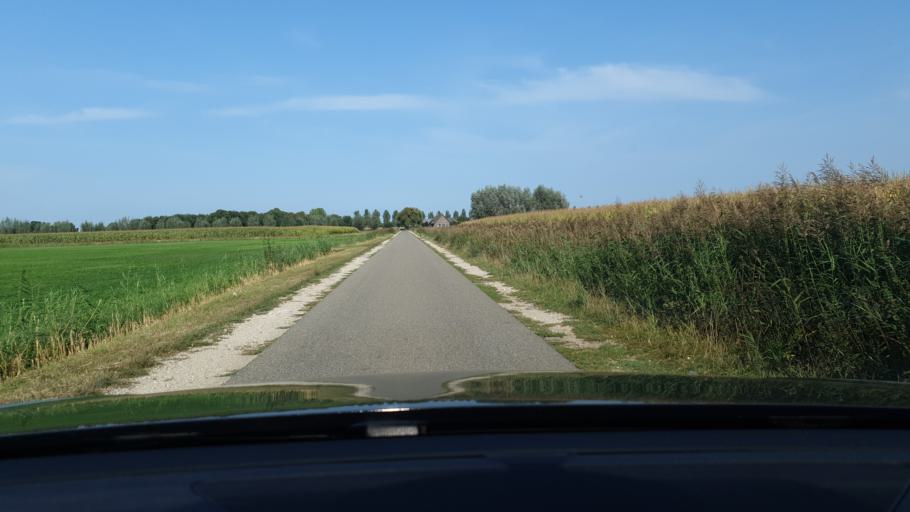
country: NL
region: North Brabant
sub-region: Gemeente Bernheze
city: Loosbroek
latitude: 51.6999
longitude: 5.4873
